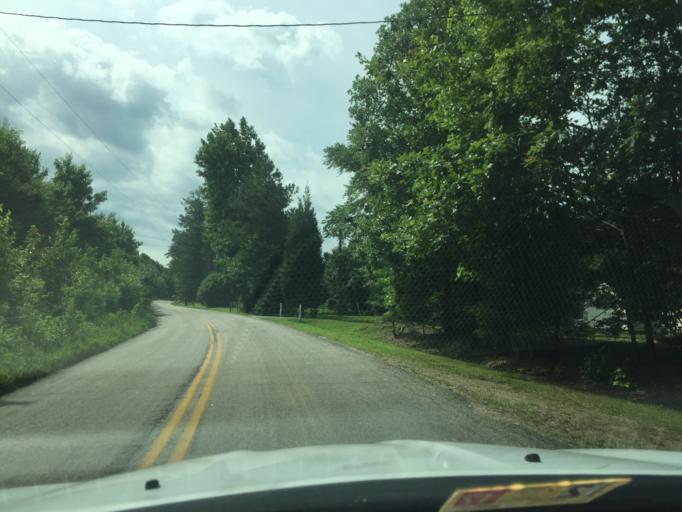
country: US
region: Virginia
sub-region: Charles City County
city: Charles City
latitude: 37.3898
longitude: -77.0150
